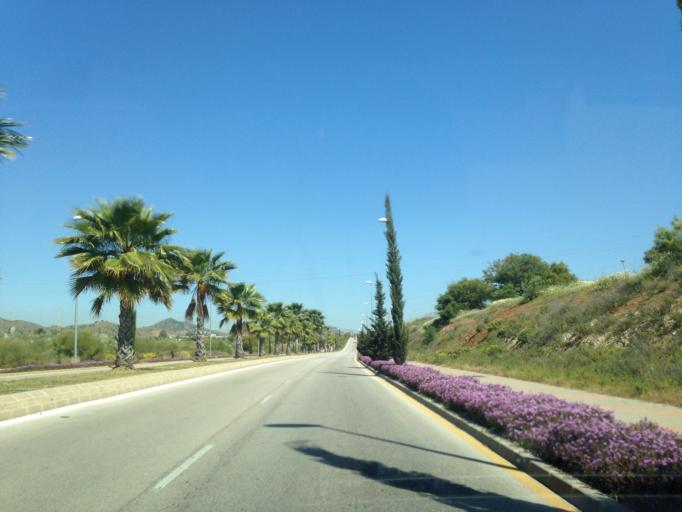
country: ES
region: Andalusia
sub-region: Provincia de Malaga
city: Malaga
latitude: 36.7260
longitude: -4.4881
